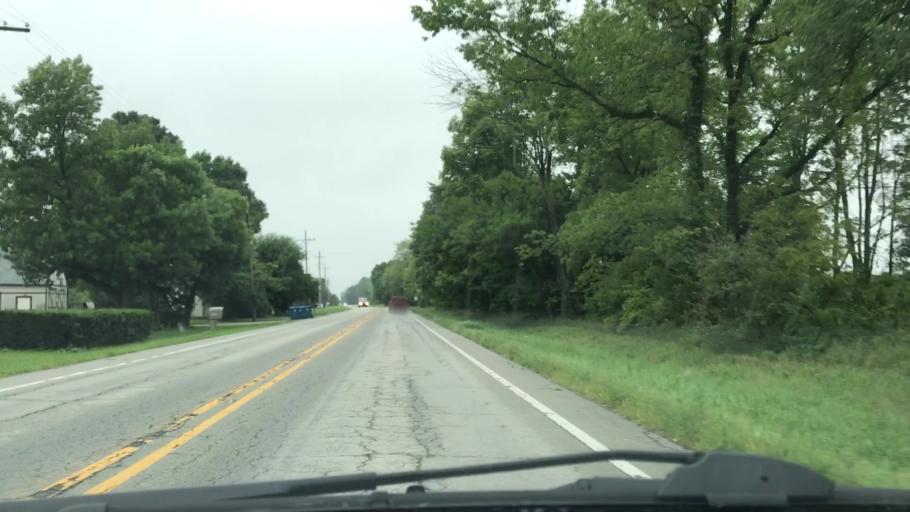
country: US
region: Indiana
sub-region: Hamilton County
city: Westfield
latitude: 40.0815
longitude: -86.0982
